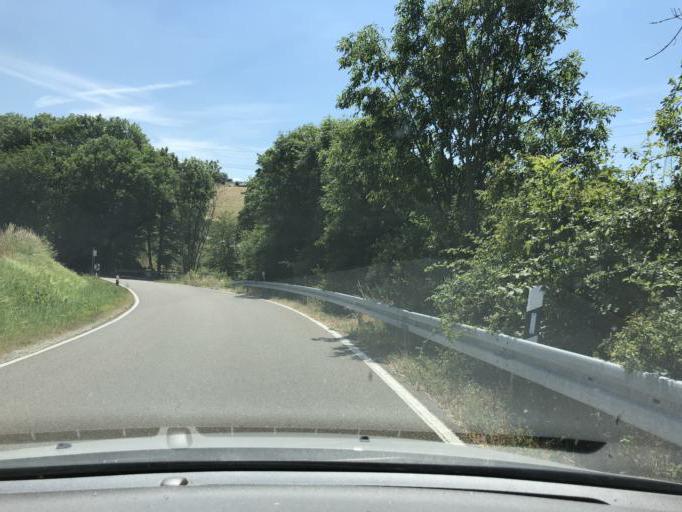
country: DE
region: Thuringia
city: Camburg
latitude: 51.0625
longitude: 11.7414
